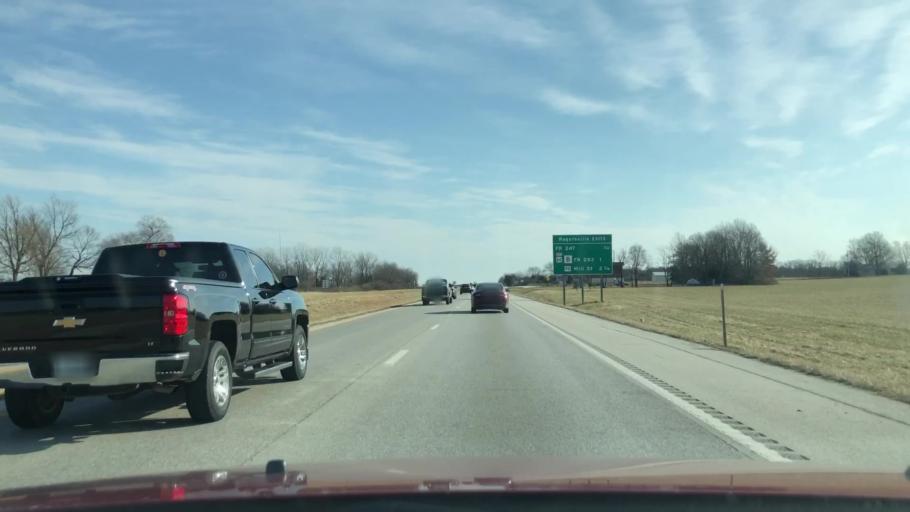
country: US
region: Missouri
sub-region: Webster County
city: Rogersville
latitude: 37.1183
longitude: -93.1040
